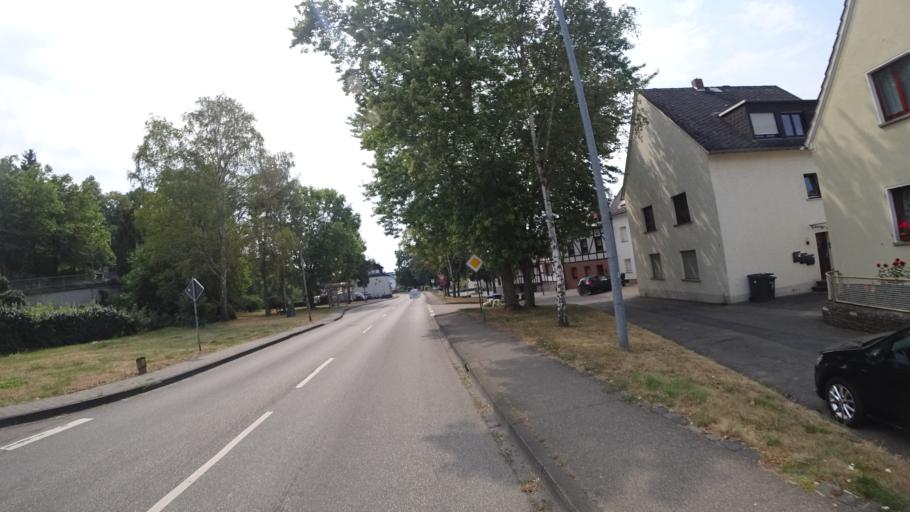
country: DE
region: Rheinland-Pfalz
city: Niederwerth
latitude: 50.4005
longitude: 7.6190
